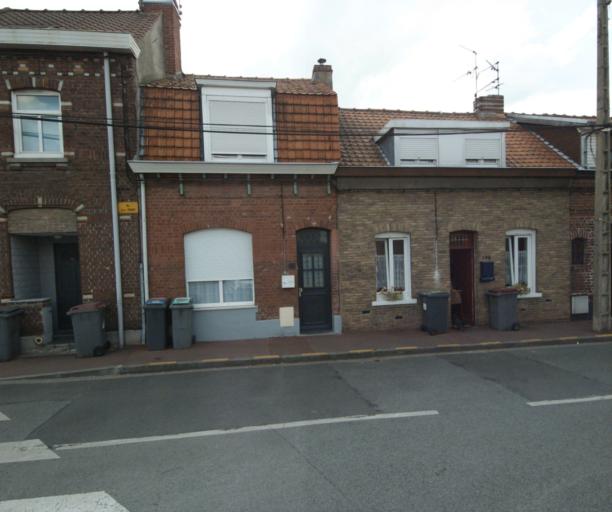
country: FR
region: Nord-Pas-de-Calais
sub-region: Departement du Nord
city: Neuville-en-Ferrain
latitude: 50.7484
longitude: 3.1517
